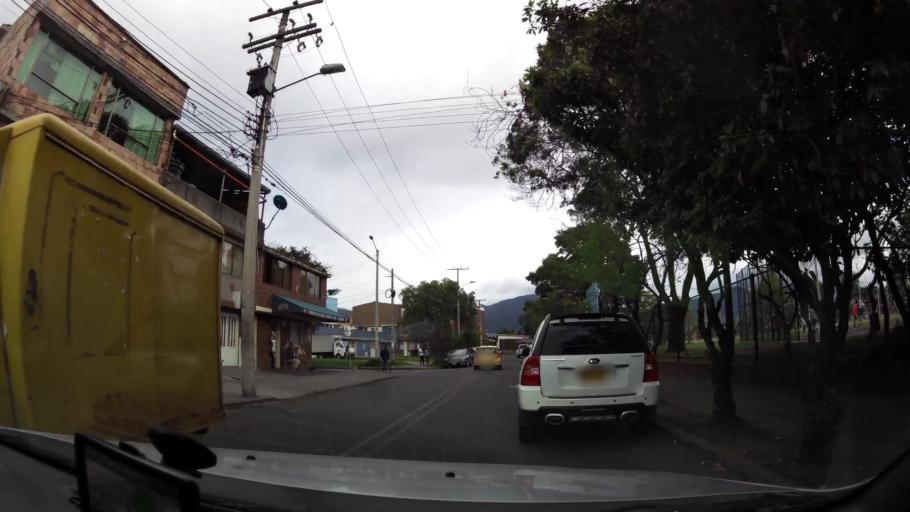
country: CO
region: Bogota D.C.
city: Bogota
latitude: 4.6102
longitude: -74.1161
